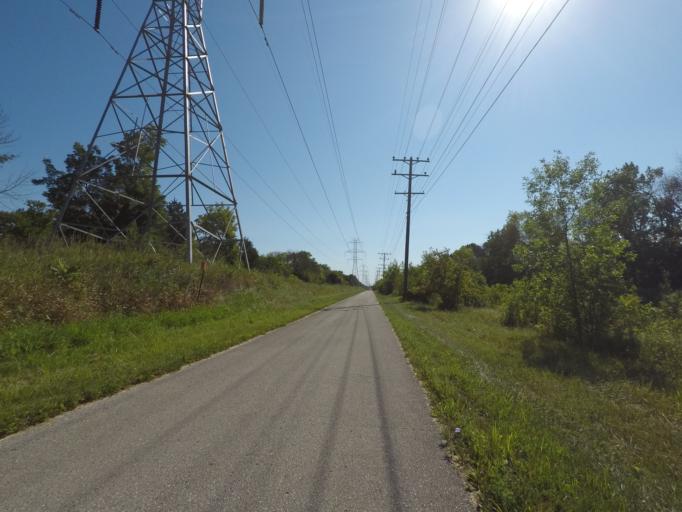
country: US
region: Wisconsin
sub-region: Waukesha County
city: Elm Grove
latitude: 43.0102
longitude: -88.0831
